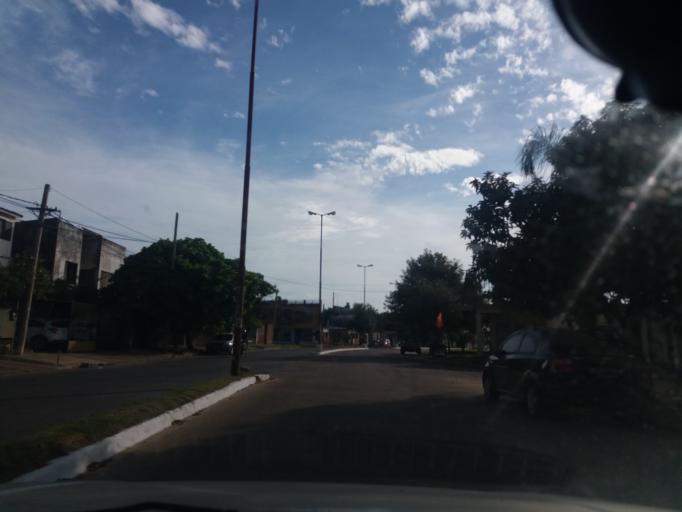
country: AR
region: Corrientes
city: Corrientes
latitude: -27.4856
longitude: -58.8337
